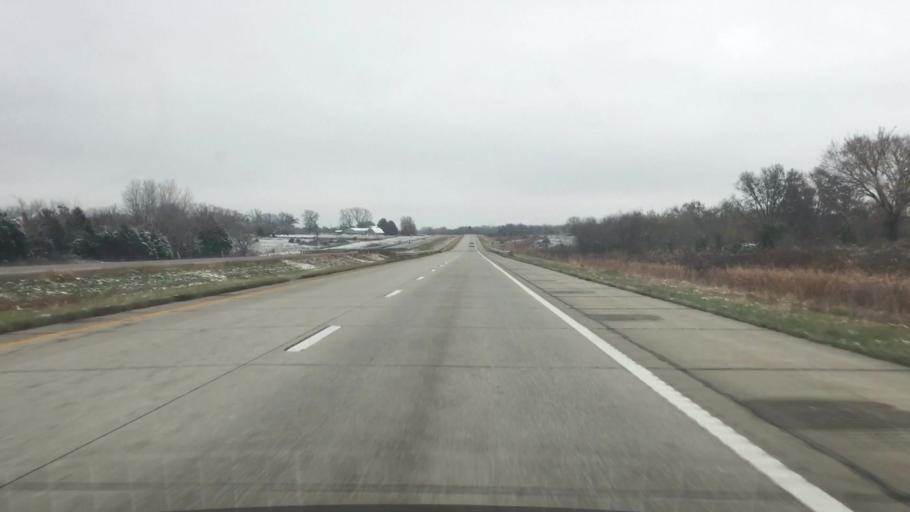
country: US
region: Missouri
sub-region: Saint Clair County
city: Osceola
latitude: 38.1965
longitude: -93.7454
